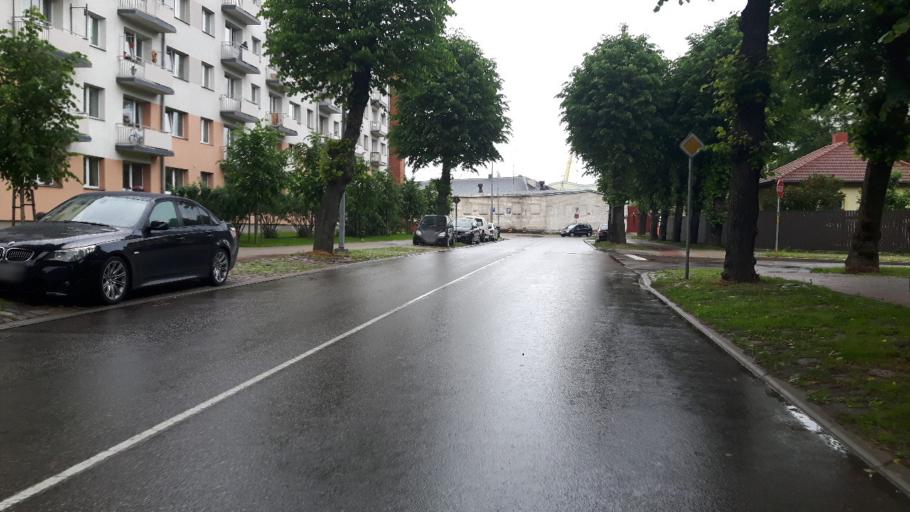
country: LV
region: Liepaja
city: Liepaja
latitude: 56.5129
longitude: 20.9981
